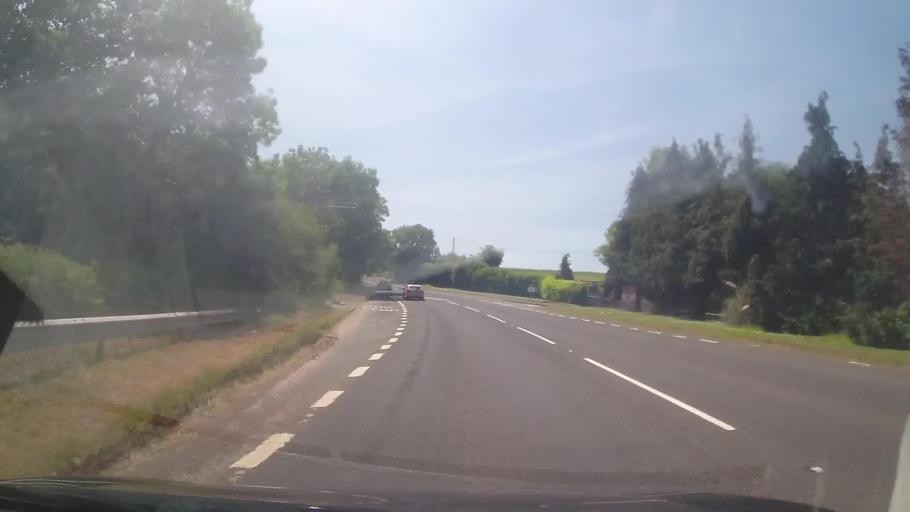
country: GB
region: England
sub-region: Herefordshire
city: Wellington
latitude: 52.0954
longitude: -2.7292
